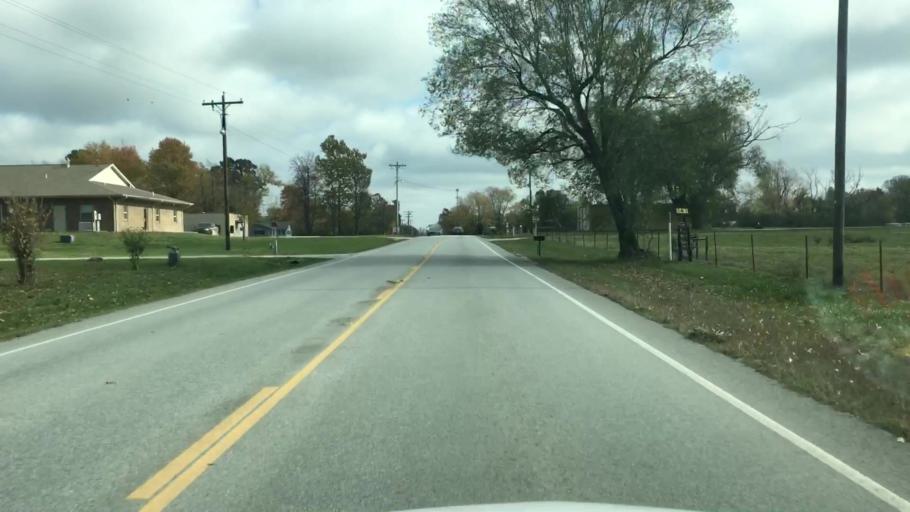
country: US
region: Arkansas
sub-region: Benton County
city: Centerton
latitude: 36.2617
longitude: -94.3595
